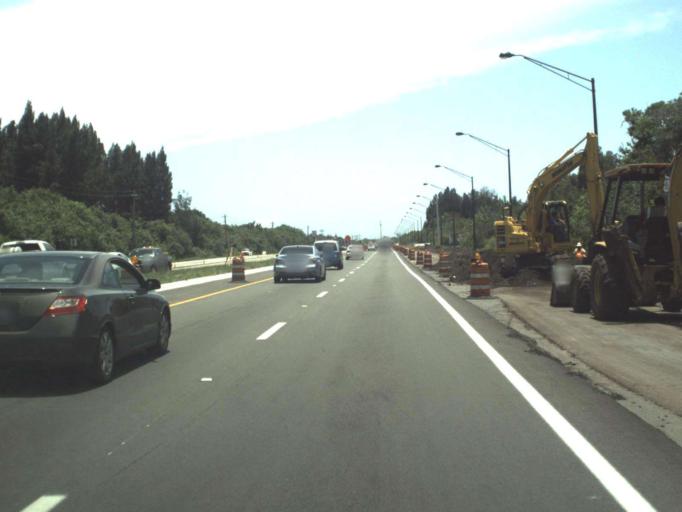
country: US
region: Florida
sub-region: Indian River County
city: Florida Ridge
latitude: 27.5757
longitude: -80.3746
